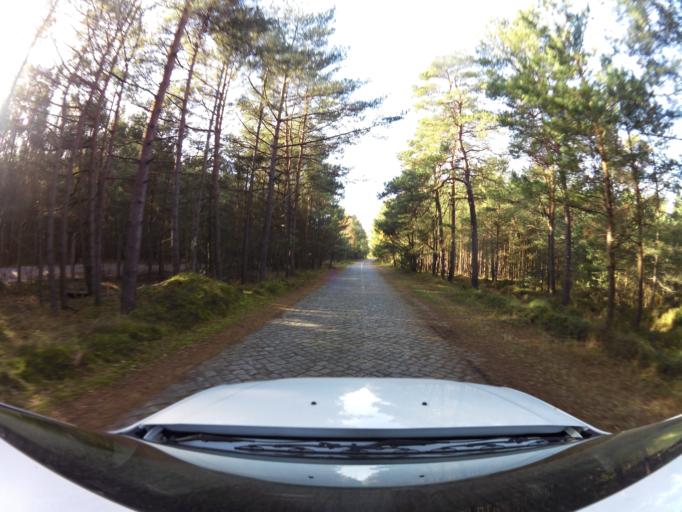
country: PL
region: West Pomeranian Voivodeship
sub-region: Powiat gryficki
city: Cerkwica
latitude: 54.1133
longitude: 15.1576
